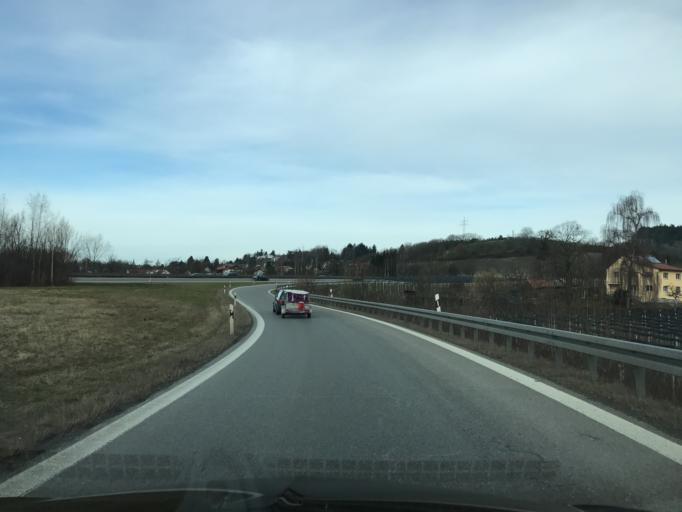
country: AT
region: Vorarlberg
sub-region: Politischer Bezirk Bregenz
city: Horbranz
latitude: 47.5508
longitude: 9.7347
